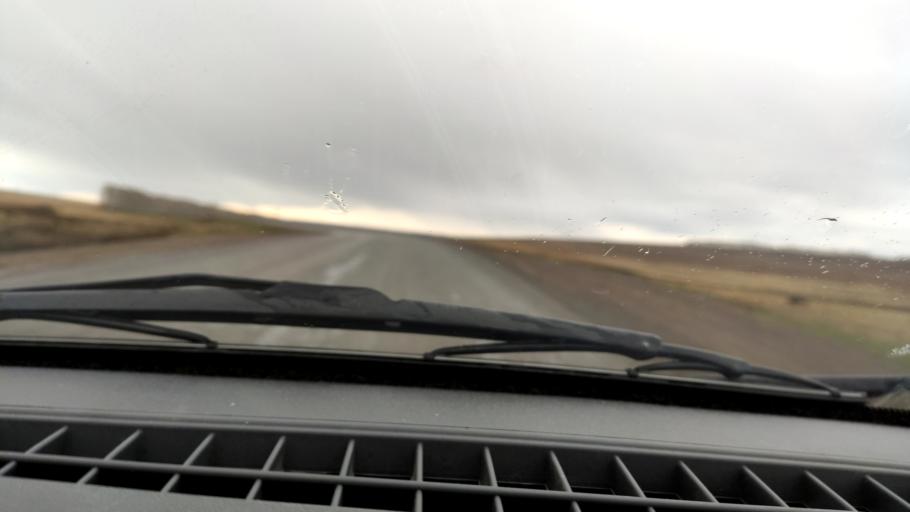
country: RU
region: Bashkortostan
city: Chekmagush
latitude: 55.1191
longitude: 54.7889
